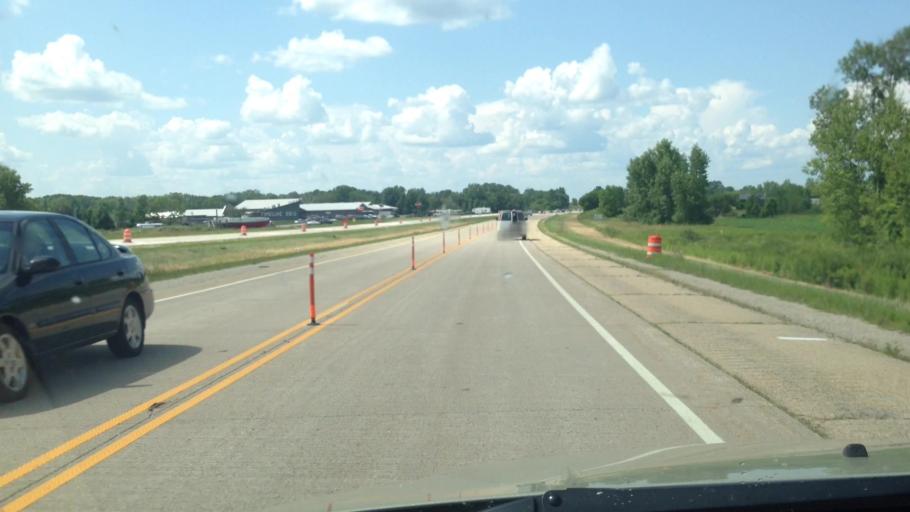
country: US
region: Wisconsin
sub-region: Shawano County
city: Bonduel
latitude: 44.7030
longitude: -88.3691
